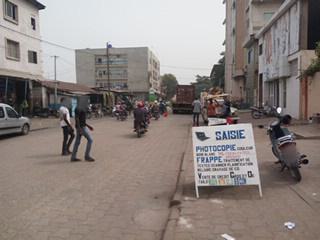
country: BJ
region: Littoral
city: Cotonou
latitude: 6.3592
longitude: 2.4259
